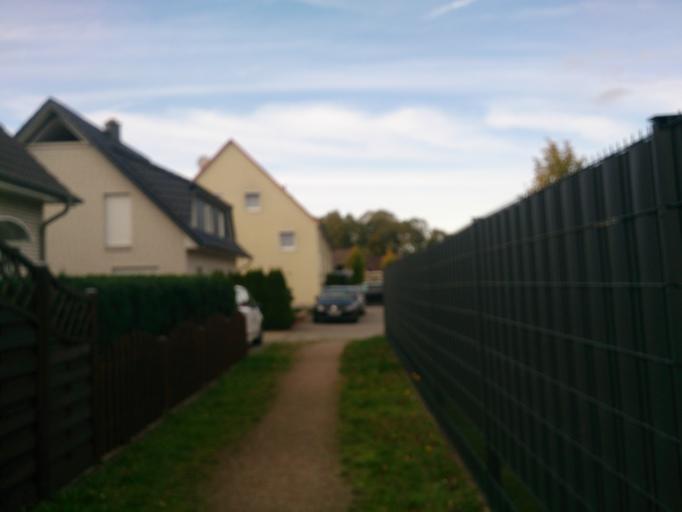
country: DE
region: Lower Saxony
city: Delmenhorst
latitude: 53.0624
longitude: 8.6353
